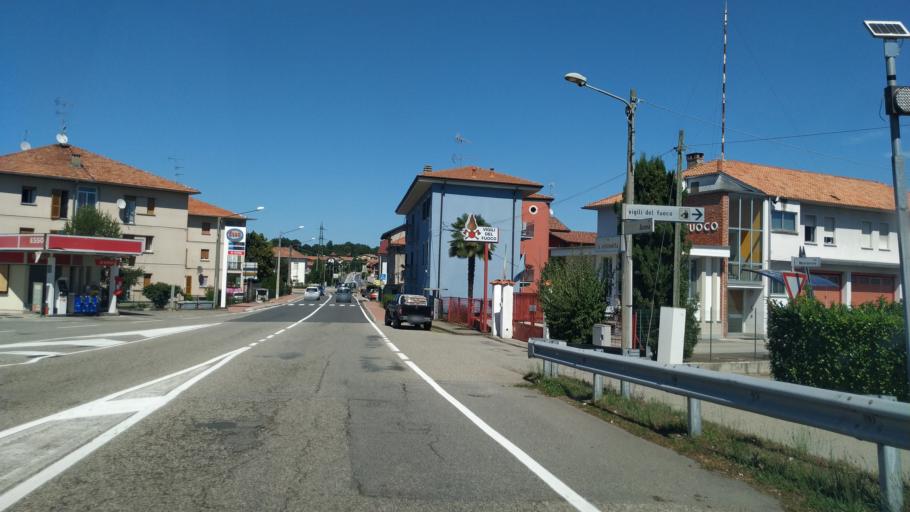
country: IT
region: Piedmont
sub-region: Provincia di Novara
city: Borgomanero
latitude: 45.7081
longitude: 8.4704
